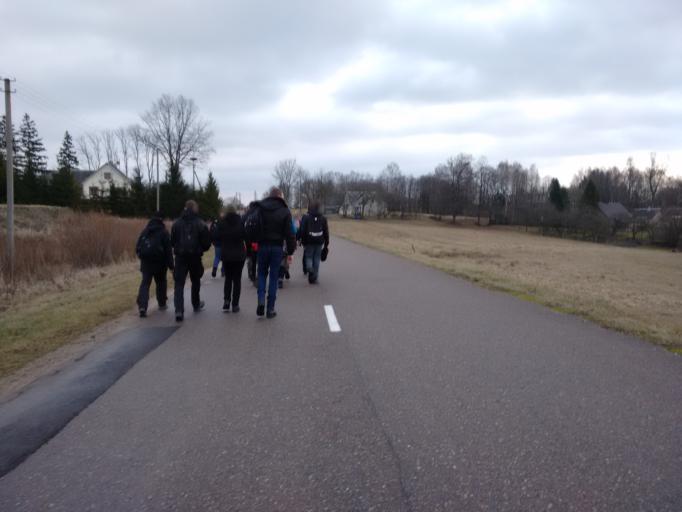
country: LT
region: Alytaus apskritis
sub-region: Alytus
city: Alytus
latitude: 54.2431
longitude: 23.8882
